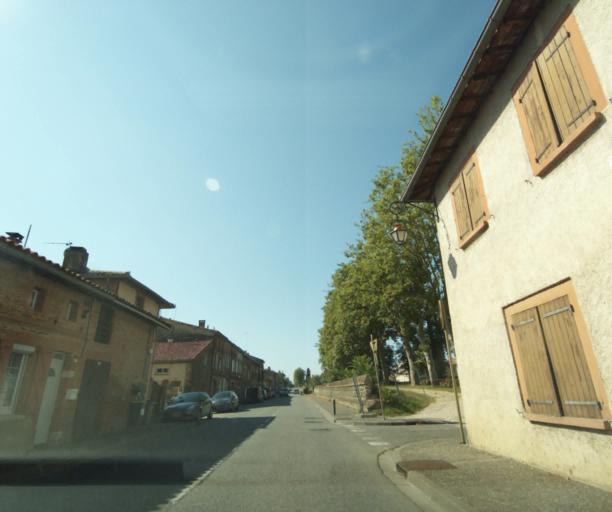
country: FR
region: Midi-Pyrenees
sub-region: Departement de la Haute-Garonne
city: Saint-Sulpice-sur-Leze
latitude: 43.3265
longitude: 1.3223
